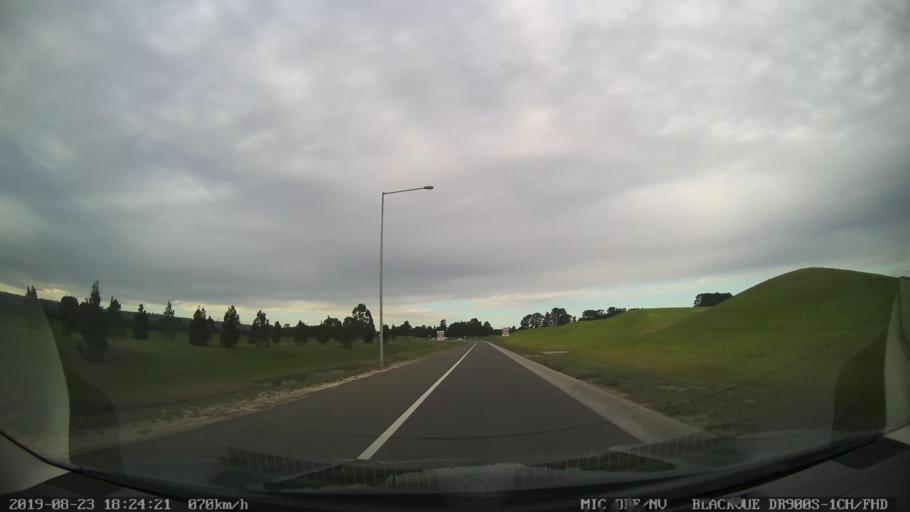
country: AU
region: Victoria
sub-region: Mornington Peninsula
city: Moorooduc
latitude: -38.2317
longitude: 145.1237
